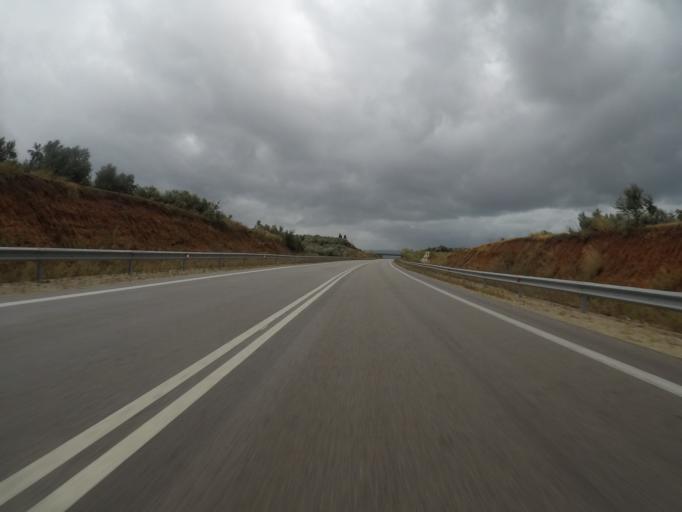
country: GR
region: Peloponnese
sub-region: Nomos Messinias
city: Gargalianoi
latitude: 37.0086
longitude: 21.6587
